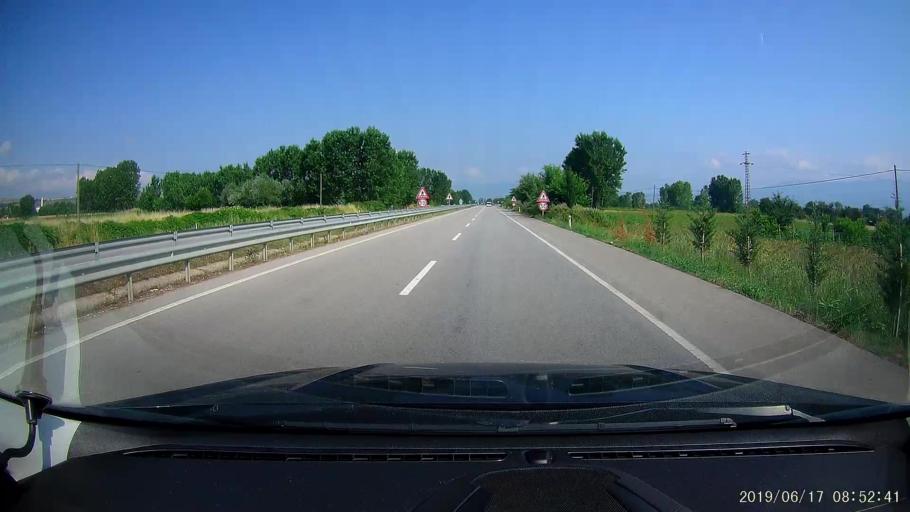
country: TR
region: Tokat
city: Erbaa
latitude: 40.7011
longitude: 36.4927
